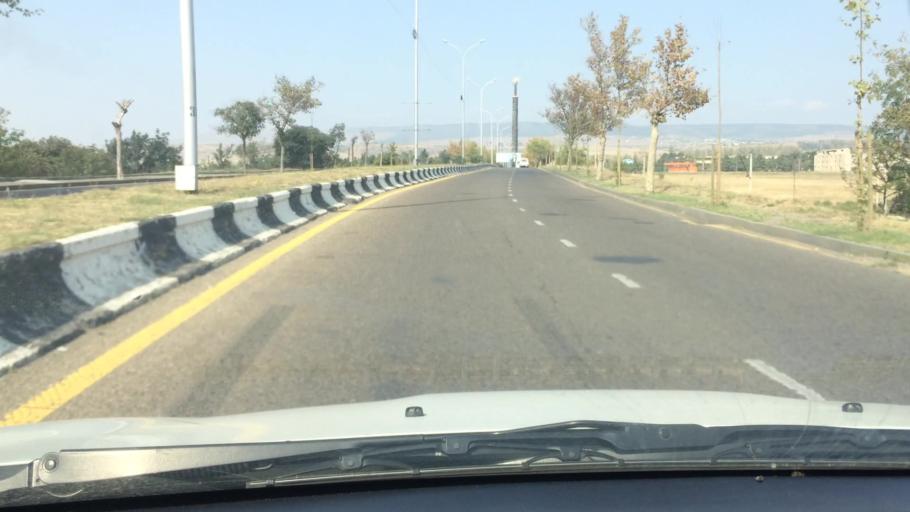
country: GE
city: Didi Lilo
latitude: 41.6854
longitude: 44.9534
